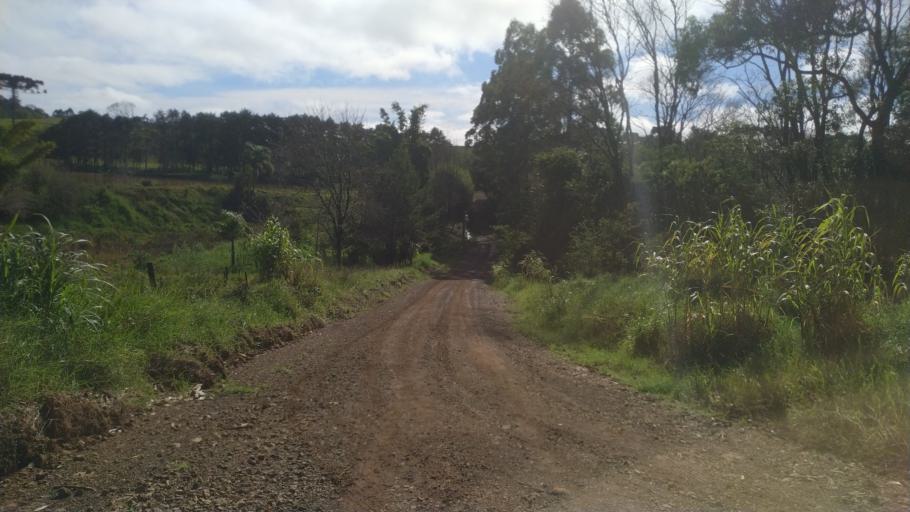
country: BR
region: Santa Catarina
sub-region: Chapeco
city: Chapeco
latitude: -27.1570
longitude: -52.5965
